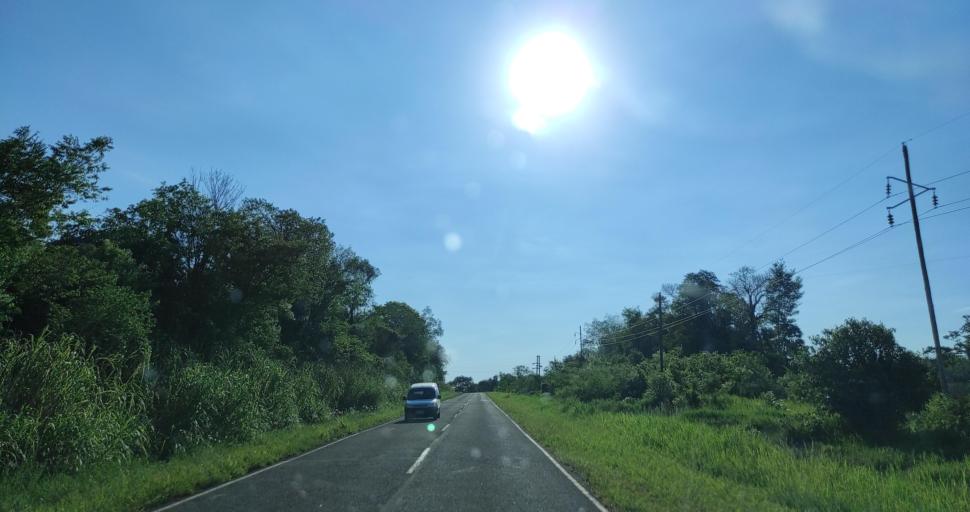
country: AR
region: Misiones
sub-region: Departamento de Eldorado
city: Eldorado
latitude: -26.3762
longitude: -54.3325
